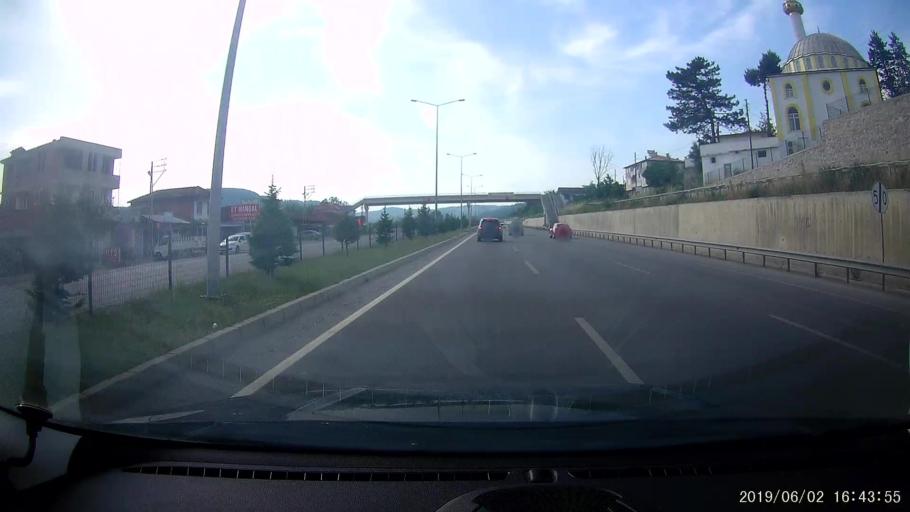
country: TR
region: Samsun
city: Kavak
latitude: 41.1427
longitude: 36.1185
